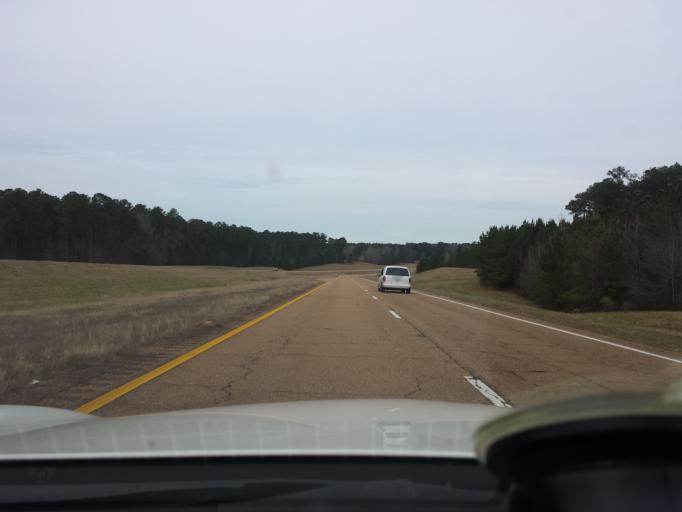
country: US
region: Mississippi
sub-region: Winston County
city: Louisville
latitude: 33.2260
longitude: -88.9814
